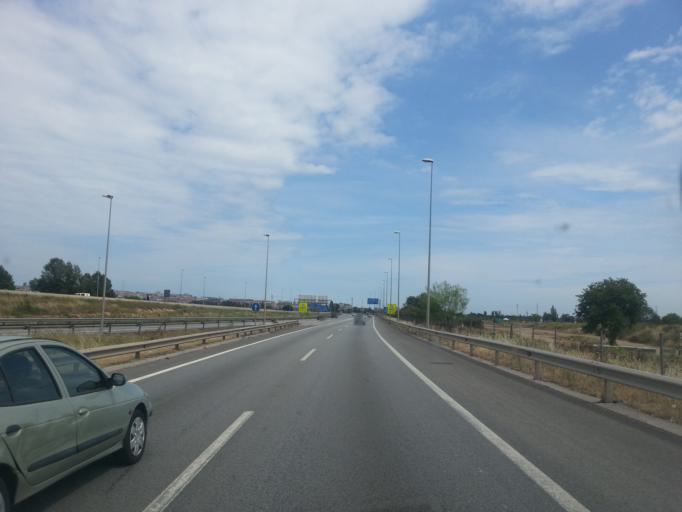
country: ES
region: Catalonia
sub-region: Provincia de Barcelona
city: Sant Feliu de Llobregat
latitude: 41.3718
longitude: 2.0368
